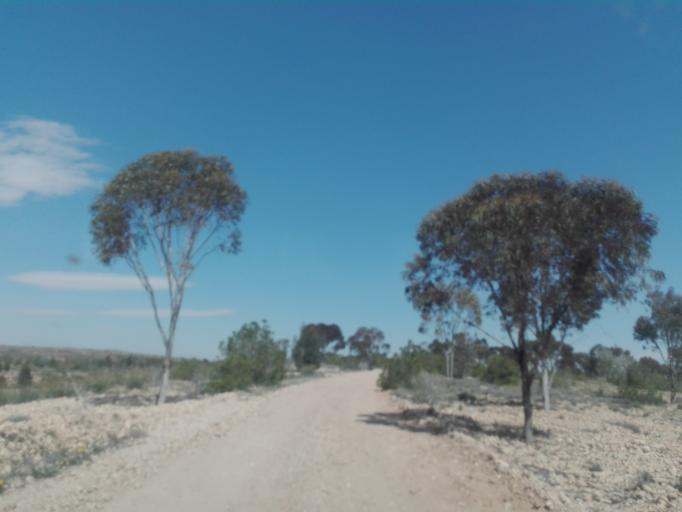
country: TN
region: Safaqis
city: Sfax
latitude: 34.7003
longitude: 10.5303
